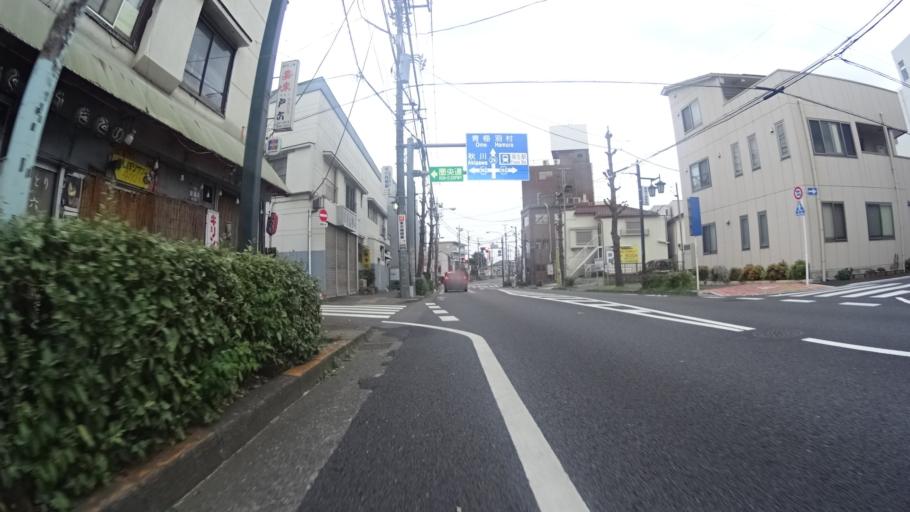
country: JP
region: Tokyo
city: Fussa
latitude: 35.7404
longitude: 139.3259
